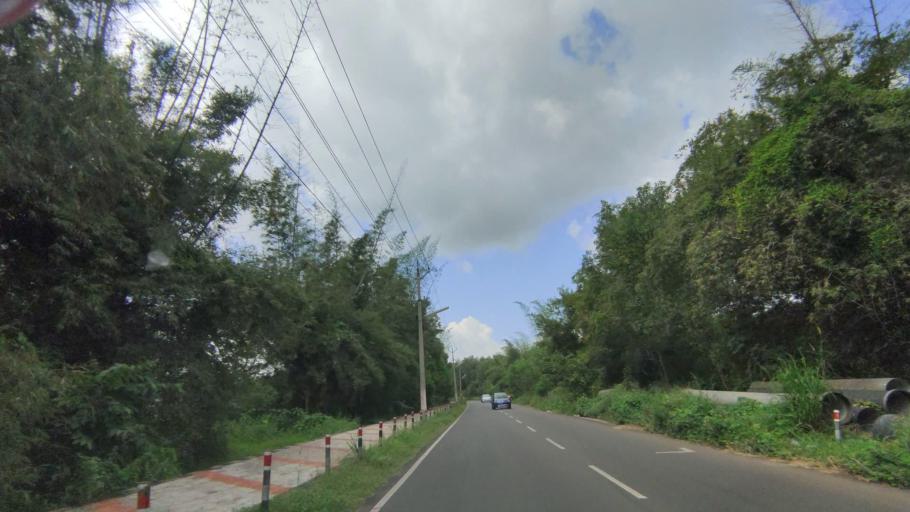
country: IN
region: Kerala
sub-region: Kottayam
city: Kottayam
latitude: 9.5702
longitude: 76.5224
